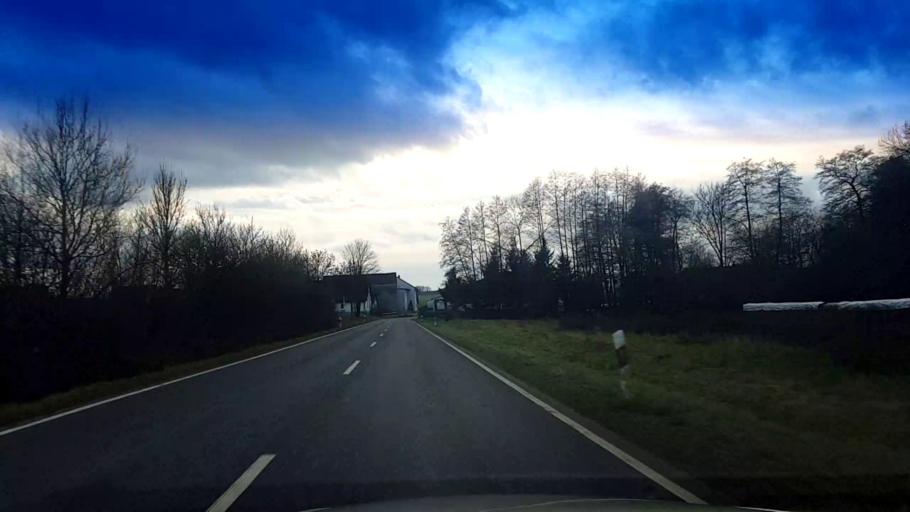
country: DE
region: Bavaria
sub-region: Upper Franconia
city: Strullendorf
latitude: 49.8591
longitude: 11.0128
